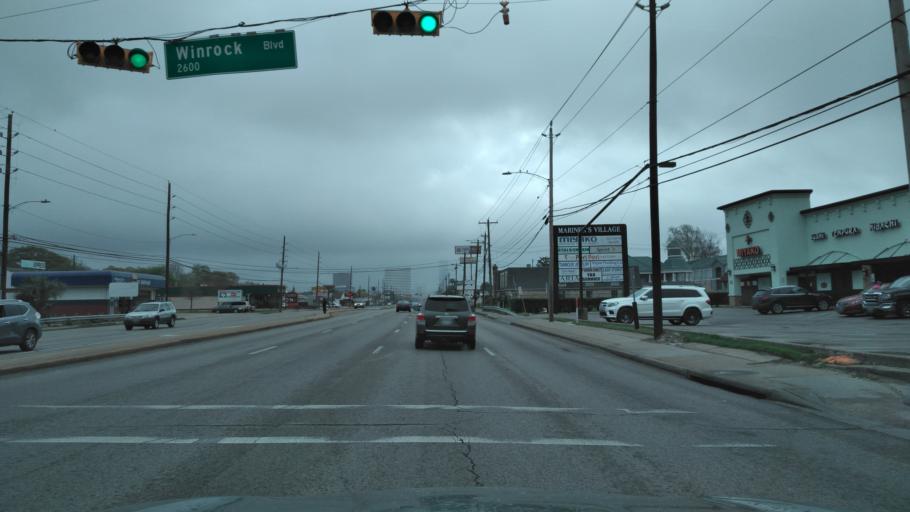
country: US
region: Texas
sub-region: Harris County
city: Piney Point Village
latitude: 29.7376
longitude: -95.4964
